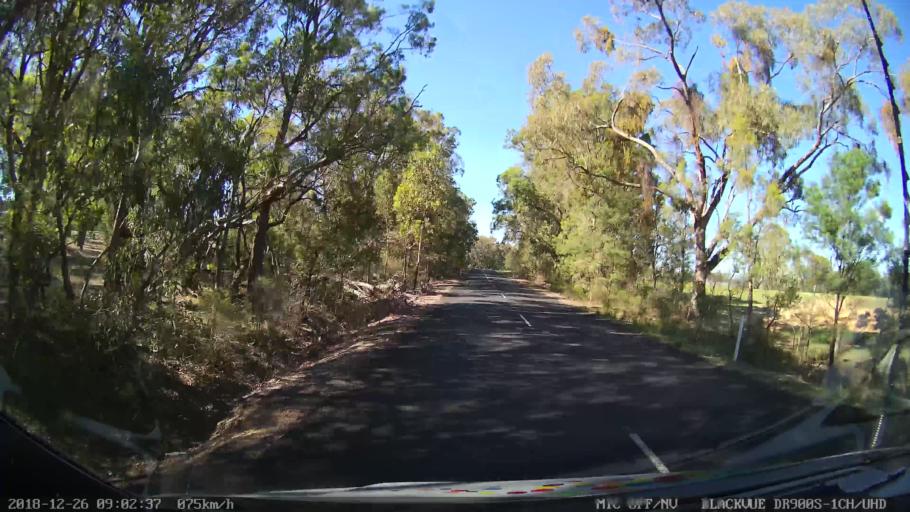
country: AU
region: New South Wales
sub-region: Mid-Western Regional
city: Kandos
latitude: -32.6548
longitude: 150.0182
